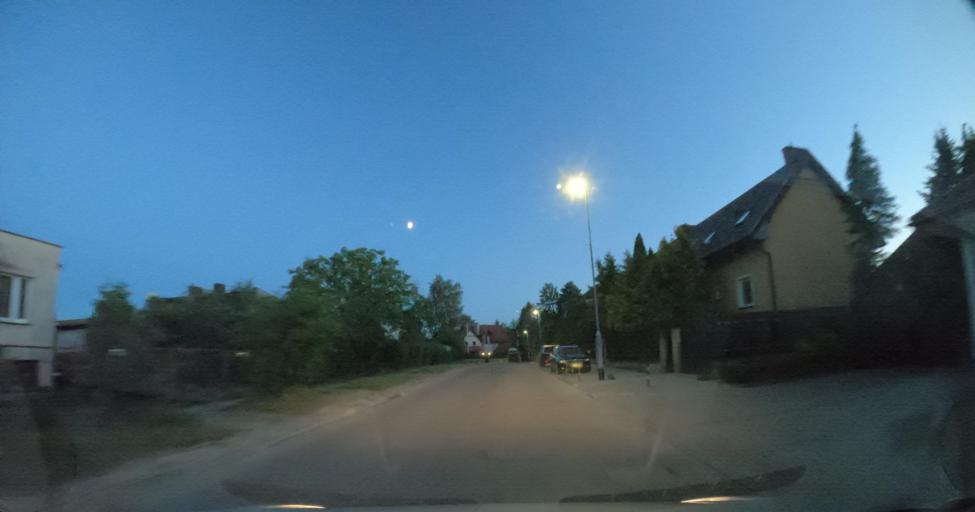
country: PL
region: Pomeranian Voivodeship
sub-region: Gdynia
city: Wielki Kack
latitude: 54.4275
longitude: 18.4664
